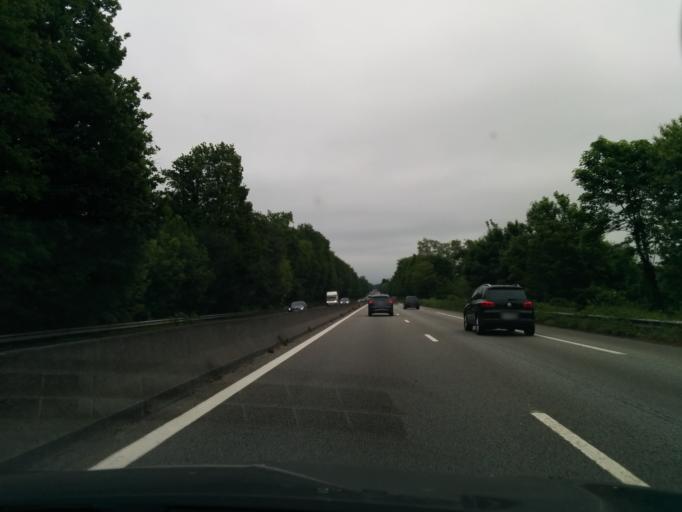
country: FR
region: Ile-de-France
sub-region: Departement des Yvelines
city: Saint-Nom-la-Breteche
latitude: 48.8659
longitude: 2.0362
